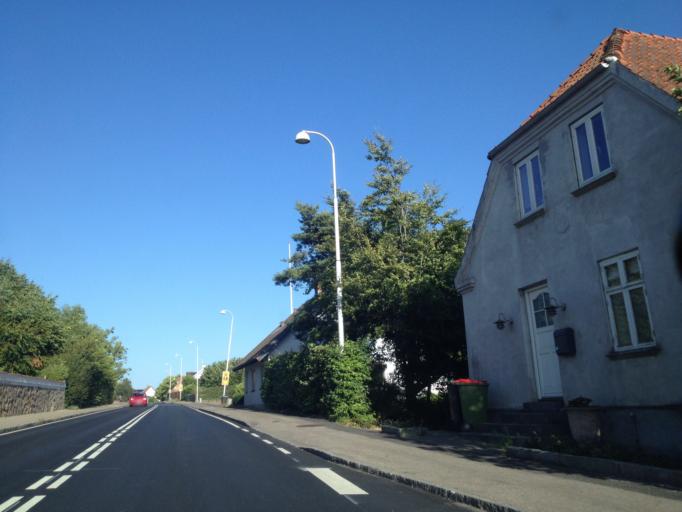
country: DK
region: Capital Region
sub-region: Gribskov Kommune
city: Helsinge
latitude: 56.0156
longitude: 12.1113
